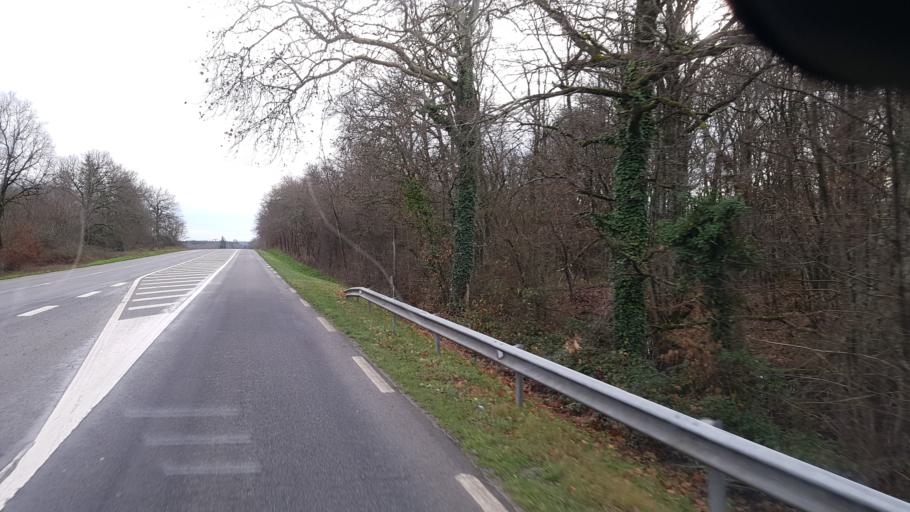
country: FR
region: Centre
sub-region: Departement du Loir-et-Cher
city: Nouan-le-Fuzelier
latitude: 47.5619
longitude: 2.0315
